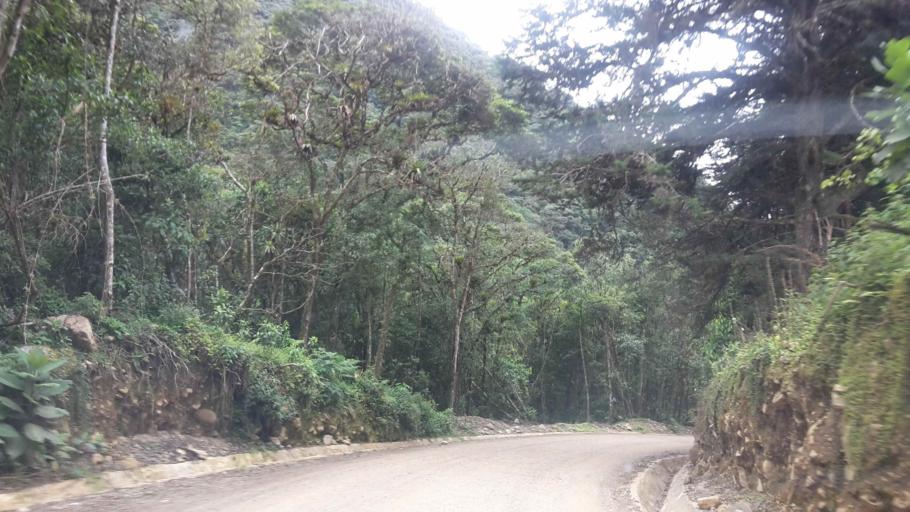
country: BO
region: Cochabamba
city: Totora
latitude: -17.5266
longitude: -65.2722
